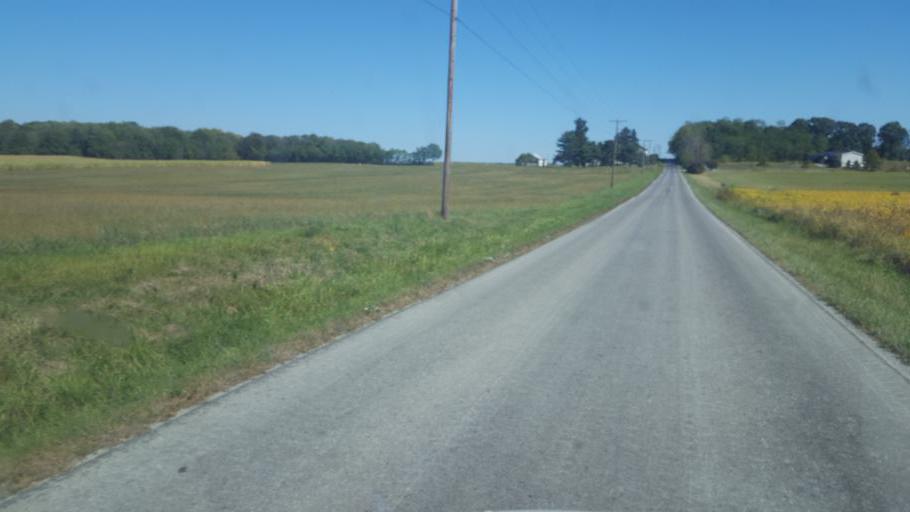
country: US
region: Ohio
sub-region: Huron County
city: Greenwich
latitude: 40.9929
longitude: -82.4770
